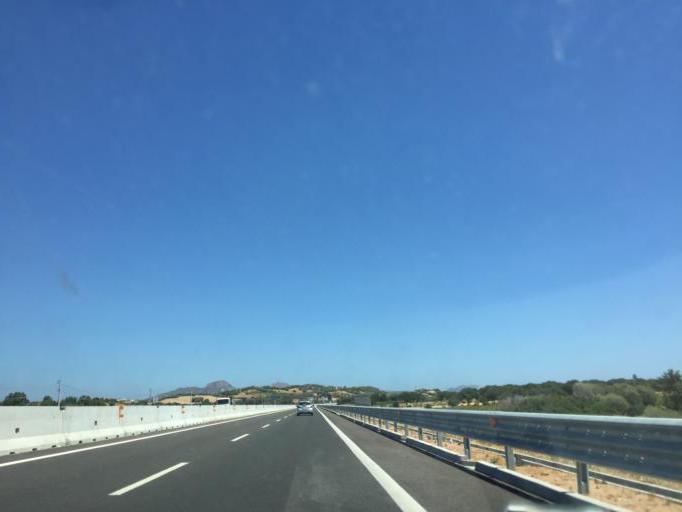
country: IT
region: Sardinia
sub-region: Provincia di Olbia-Tempio
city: Loiri Porto San Paolo
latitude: 40.8754
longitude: 9.4623
